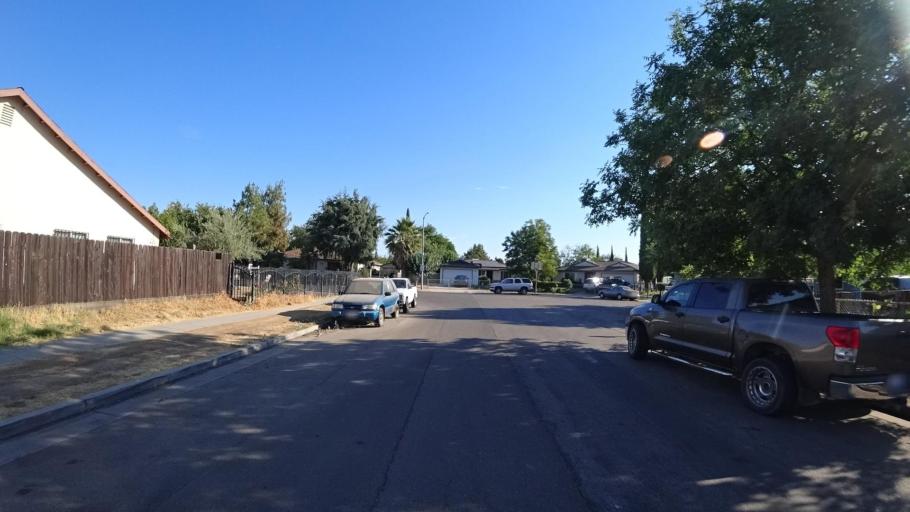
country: US
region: California
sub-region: Fresno County
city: Fresno
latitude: 36.7147
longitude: -119.7437
